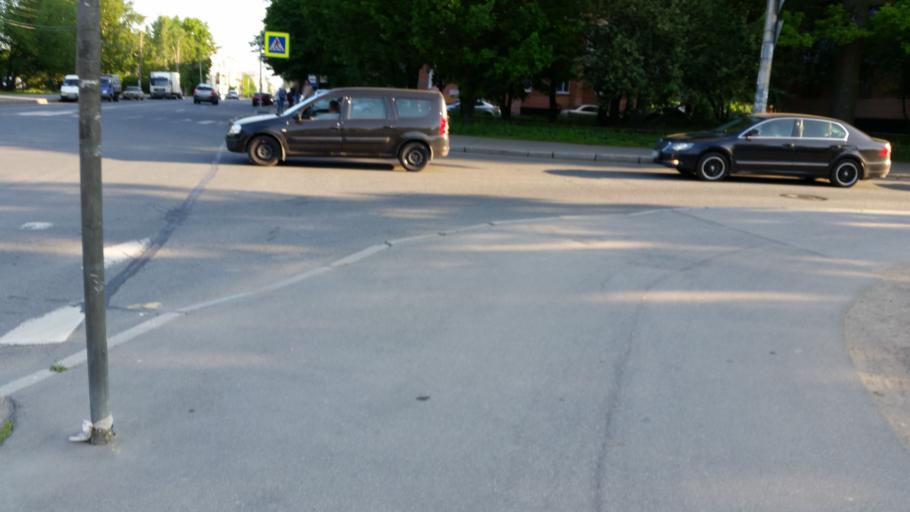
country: RU
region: St.-Petersburg
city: Sosnovaya Polyana
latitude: 59.8450
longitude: 30.1468
